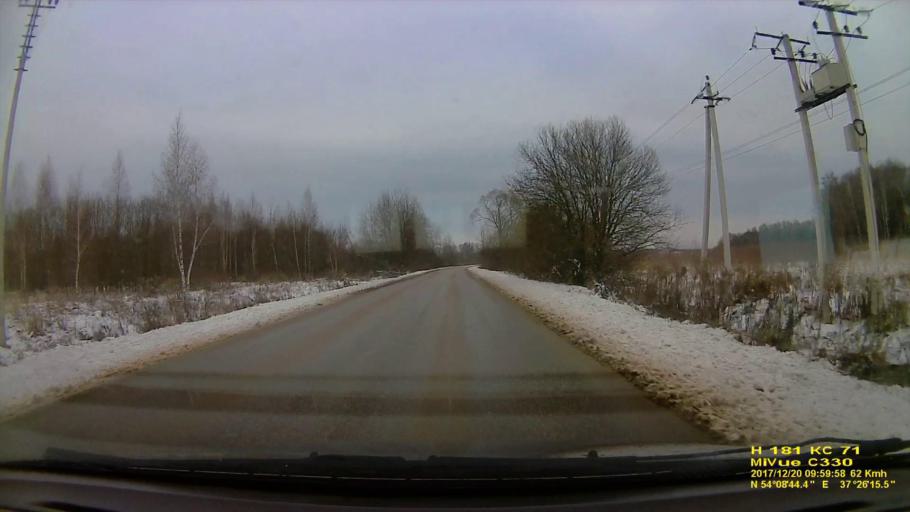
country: RU
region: Tula
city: Kosaya Gora
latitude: 54.1455
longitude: 37.4377
